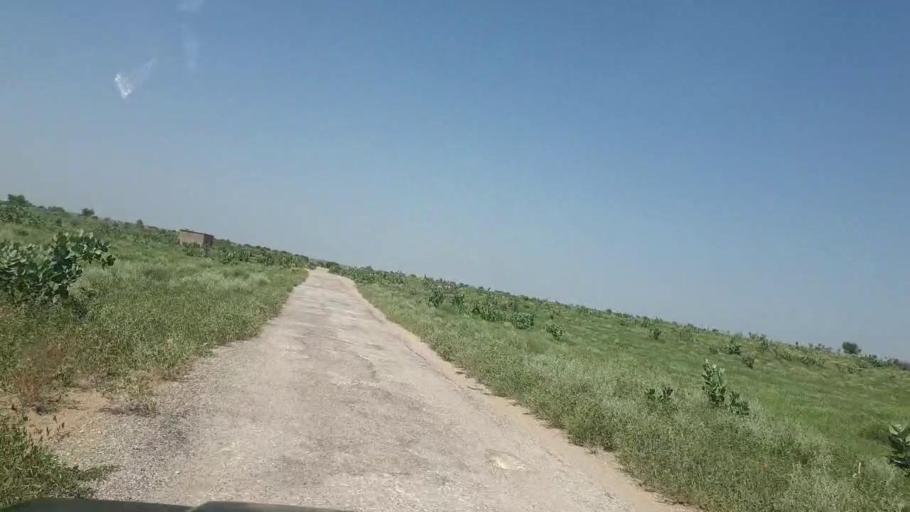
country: PK
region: Sindh
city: Chor
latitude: 25.3600
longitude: 70.3290
